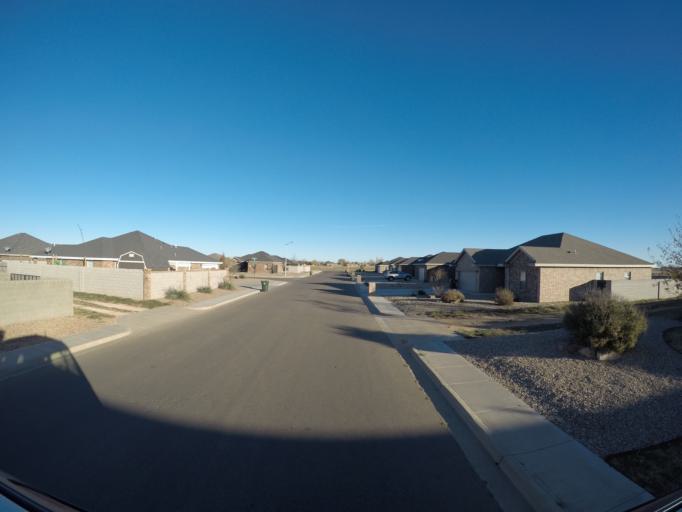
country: US
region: New Mexico
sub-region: Curry County
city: Clovis
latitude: 34.4084
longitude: -103.1689
